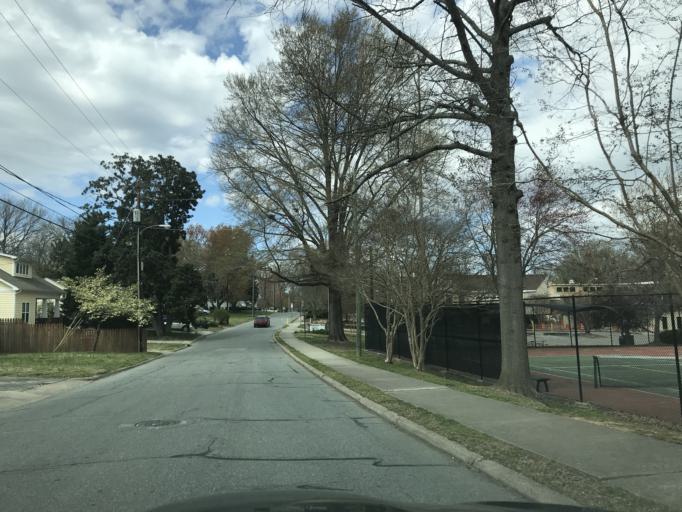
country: US
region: North Carolina
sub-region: Orange County
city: Chapel Hill
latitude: 35.9119
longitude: -79.0641
